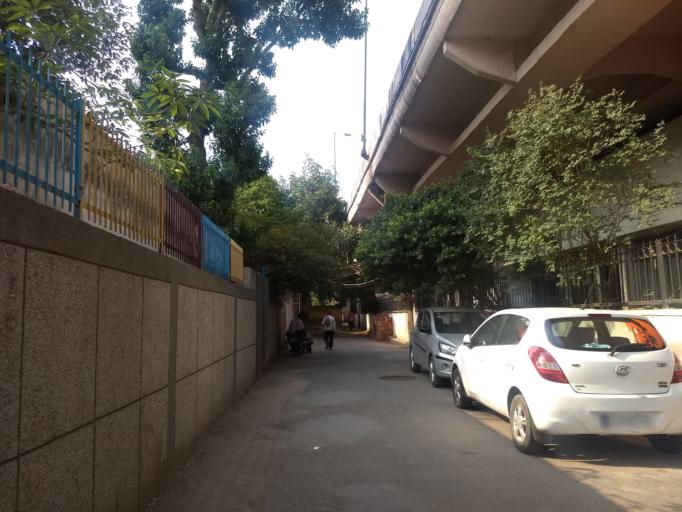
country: IN
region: NCT
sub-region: New Delhi
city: New Delhi
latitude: 28.5780
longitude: 77.2292
